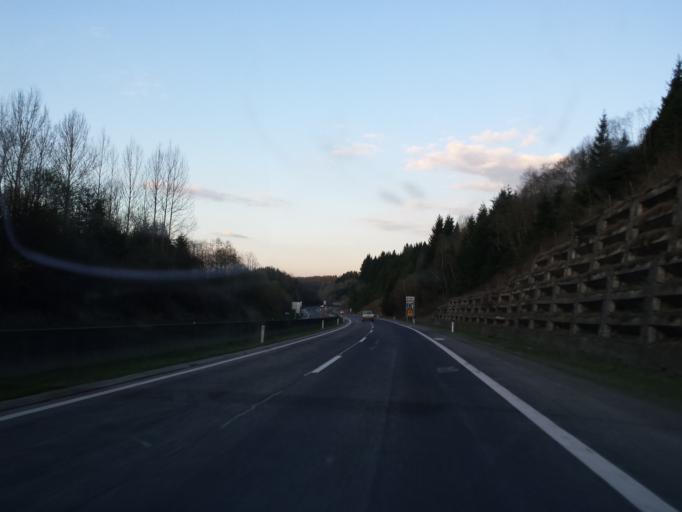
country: AT
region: Styria
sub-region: Politischer Bezirk Bruck-Muerzzuschlag
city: Mitterdorf im Muerztal
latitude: 47.5213
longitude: 15.4991
